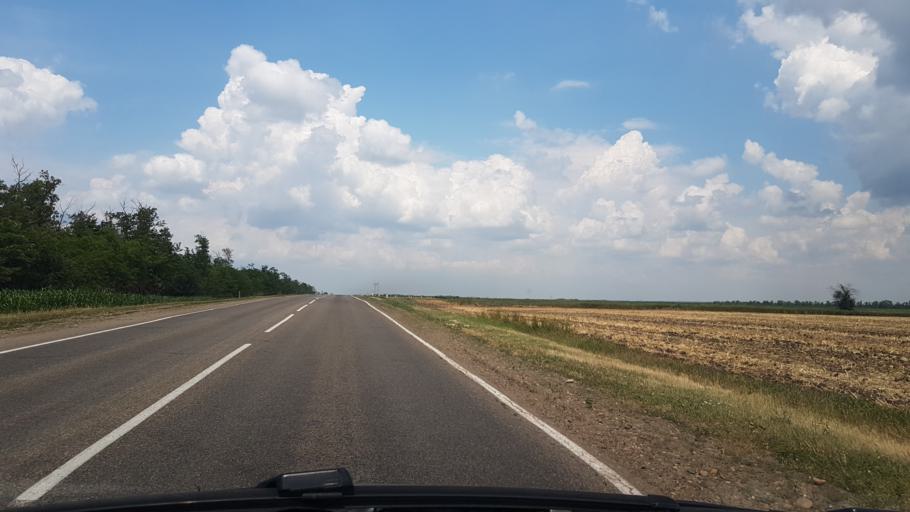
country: RU
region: Krasnodarskiy
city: Dmitriyevskaya
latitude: 45.6787
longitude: 40.7440
